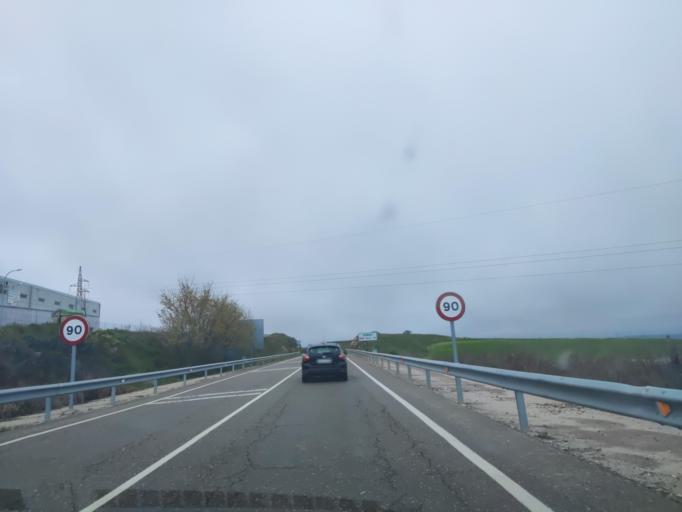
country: ES
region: Castille-La Mancha
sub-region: Province of Toledo
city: Bargas
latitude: 39.9463
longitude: -4.0212
